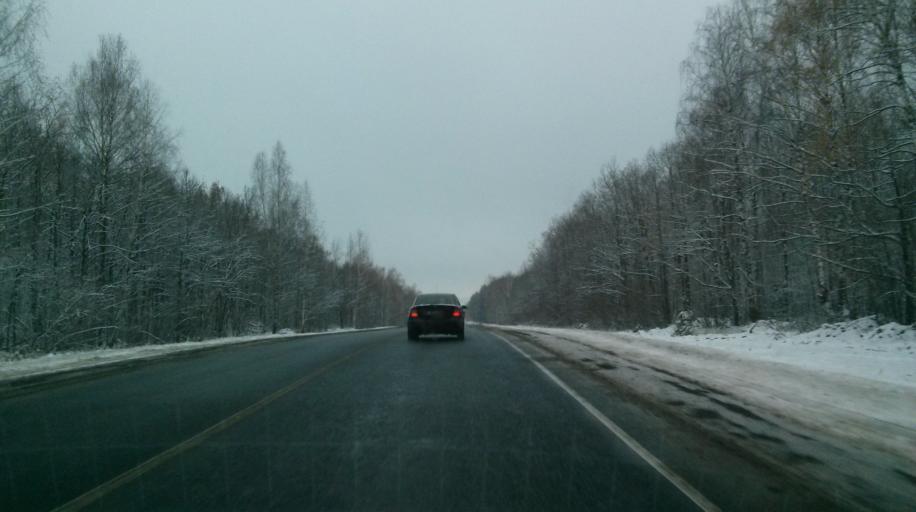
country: RU
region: Nizjnij Novgorod
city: Vorsma
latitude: 56.0037
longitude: 43.3191
